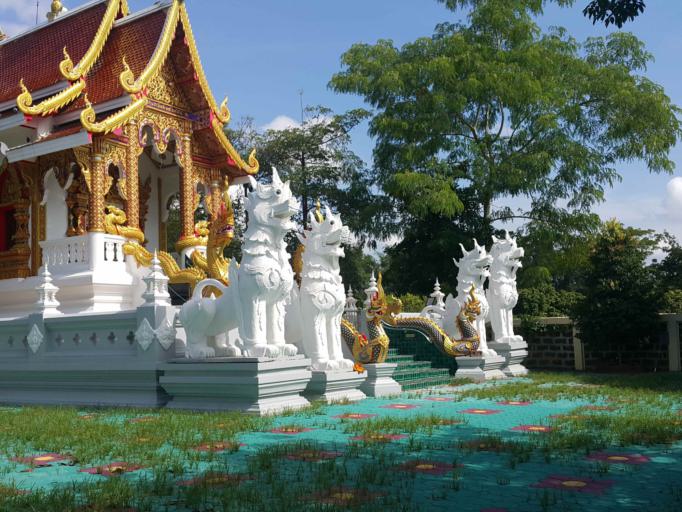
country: TH
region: Chiang Mai
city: San Kamphaeng
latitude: 18.8019
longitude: 99.0924
